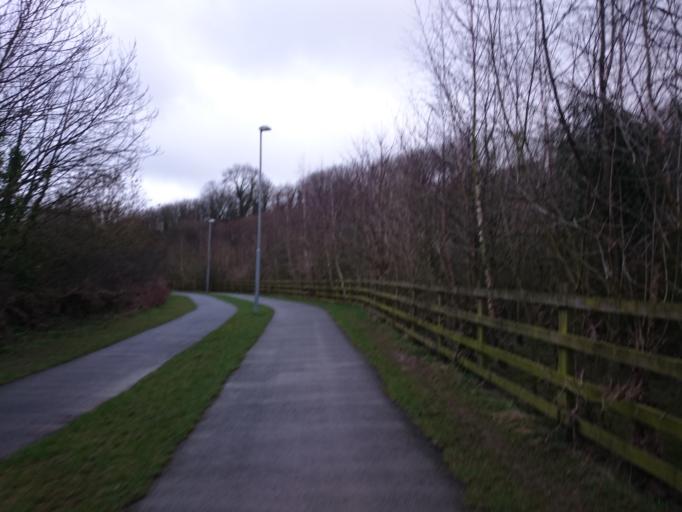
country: IE
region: Leinster
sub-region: Kilkenny
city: Kilkenny
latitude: 52.6687
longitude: -7.2618
